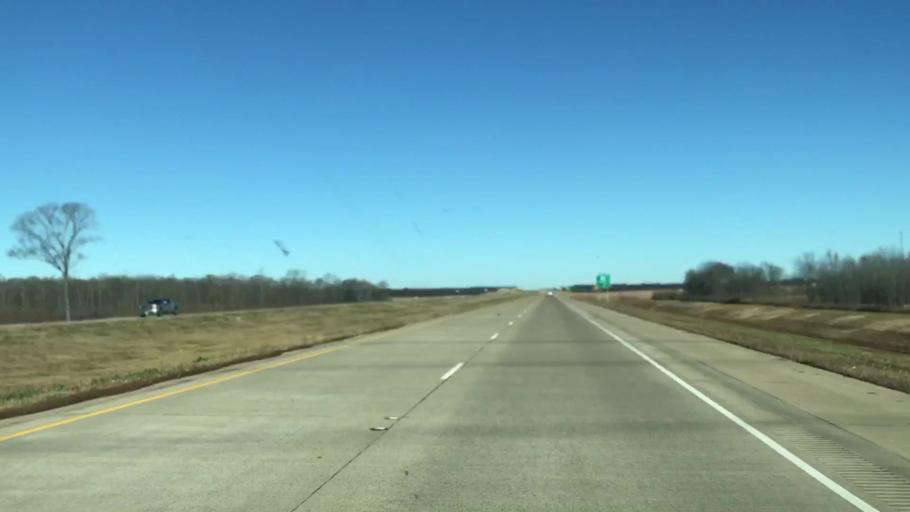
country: US
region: Louisiana
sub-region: Caddo Parish
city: Blanchard
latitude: 32.6674
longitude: -93.8469
